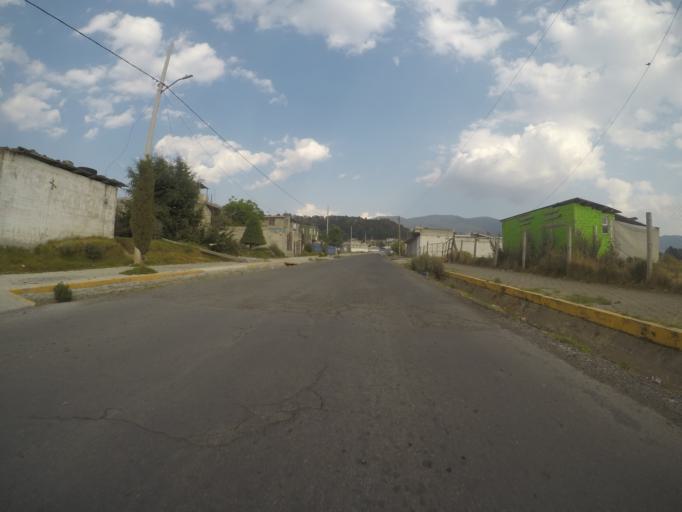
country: MX
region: Mexico
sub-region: Xalatlaco
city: El Aguila (La Mesa)
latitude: 19.1580
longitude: -99.4018
